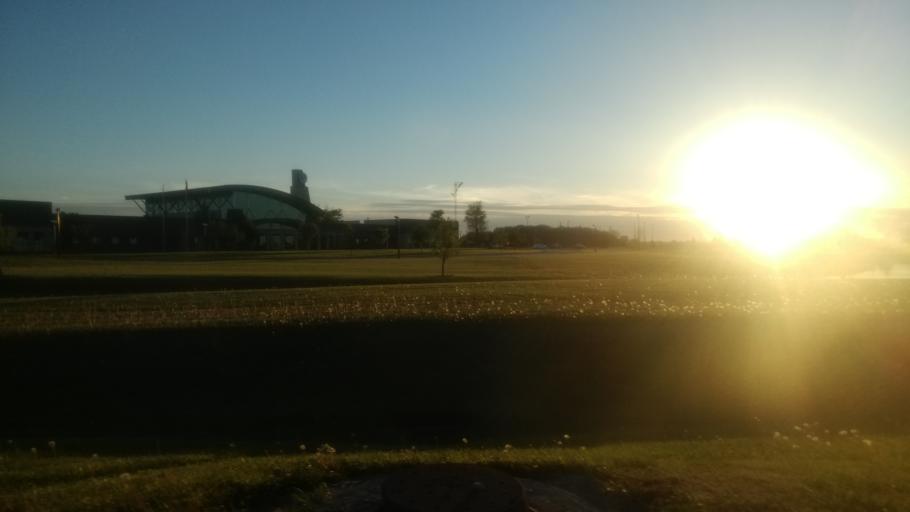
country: US
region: Ohio
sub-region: Hancock County
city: Findlay
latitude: 41.0790
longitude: -83.6179
